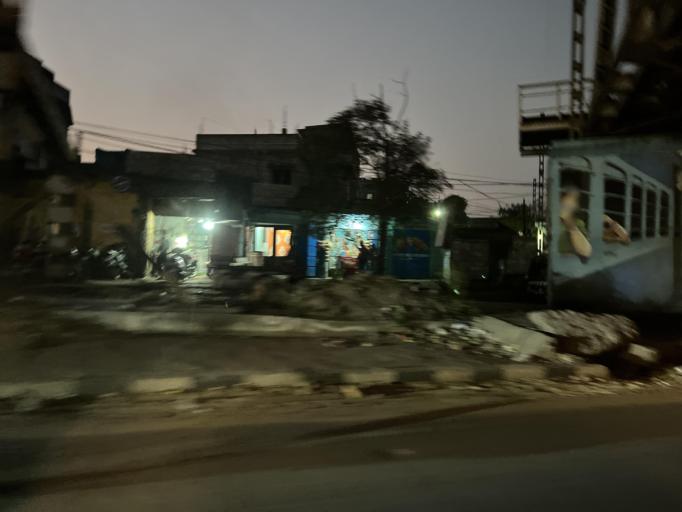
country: IN
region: Odisha
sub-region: Cuttack
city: Cuttack
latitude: 20.4502
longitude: 85.8986
